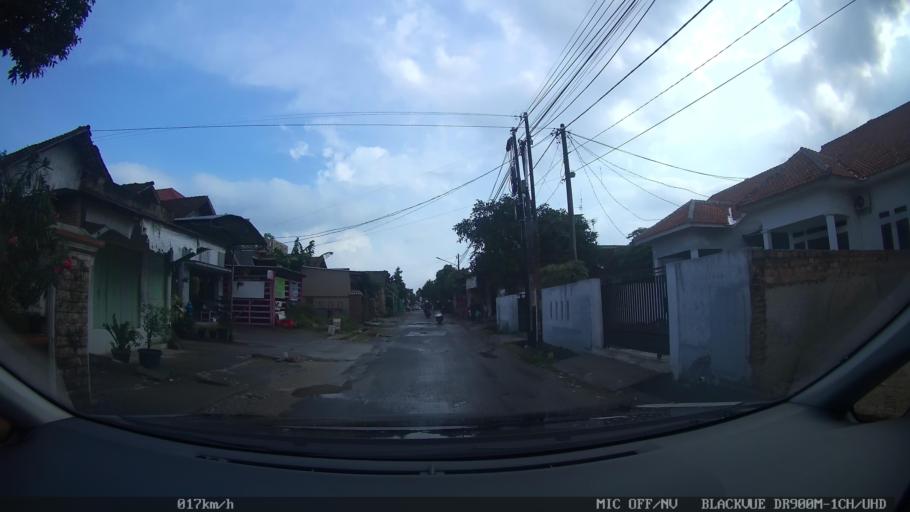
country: ID
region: Lampung
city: Kedaton
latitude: -5.3892
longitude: 105.2975
